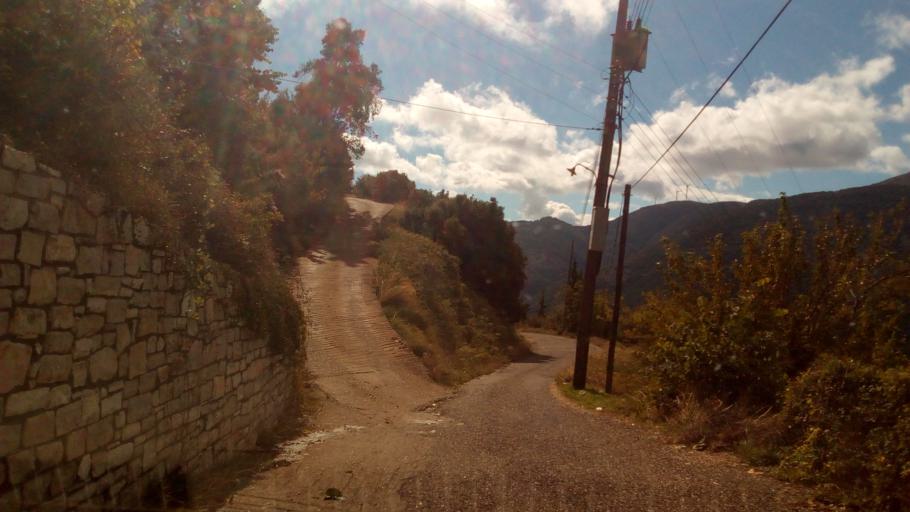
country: GR
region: West Greece
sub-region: Nomos Aitolias kai Akarnanias
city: Nafpaktos
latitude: 38.4909
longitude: 21.8522
